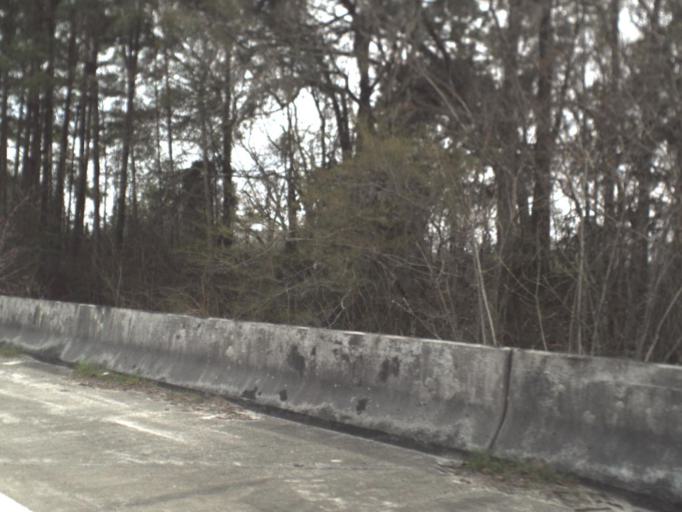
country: US
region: Florida
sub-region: Gadsden County
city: Quincy
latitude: 30.3848
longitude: -84.6521
